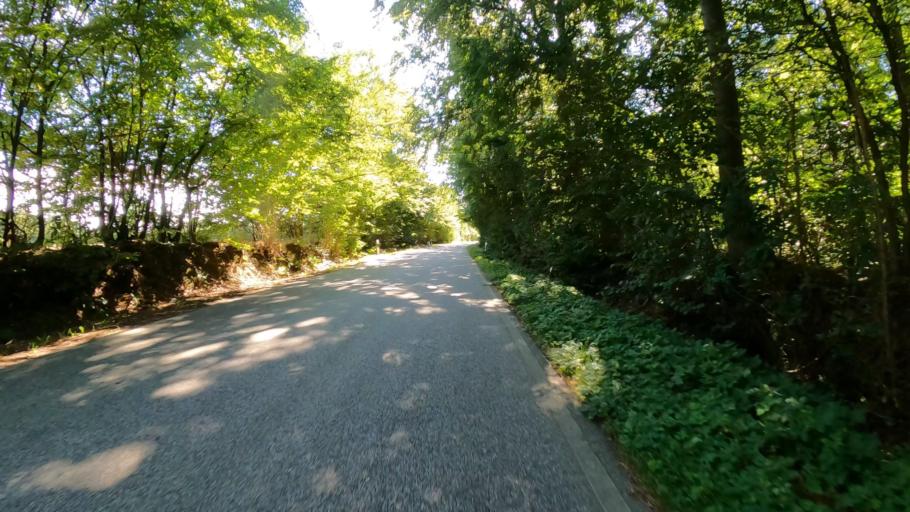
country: DE
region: Schleswig-Holstein
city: Hamberge
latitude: 53.8140
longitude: 10.5861
